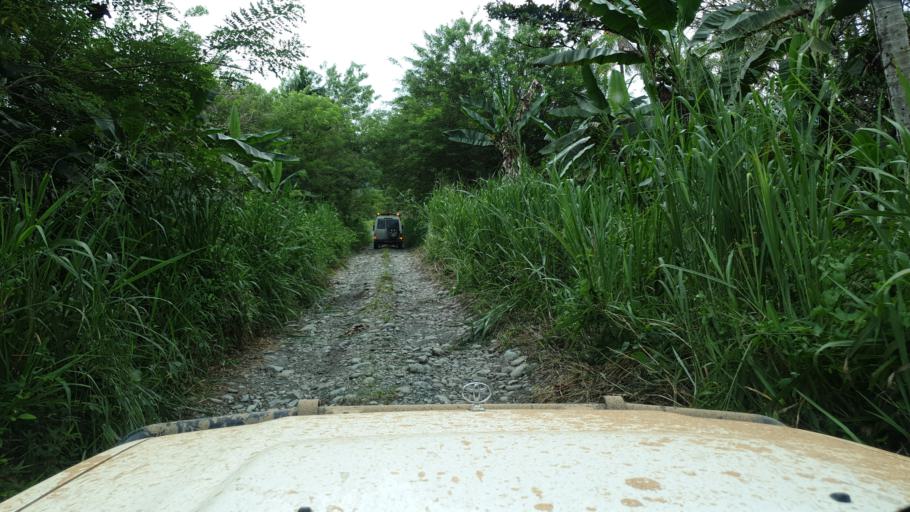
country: PG
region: Northern Province
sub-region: Sohe
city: Kokoda
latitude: -8.9313
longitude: 147.8681
